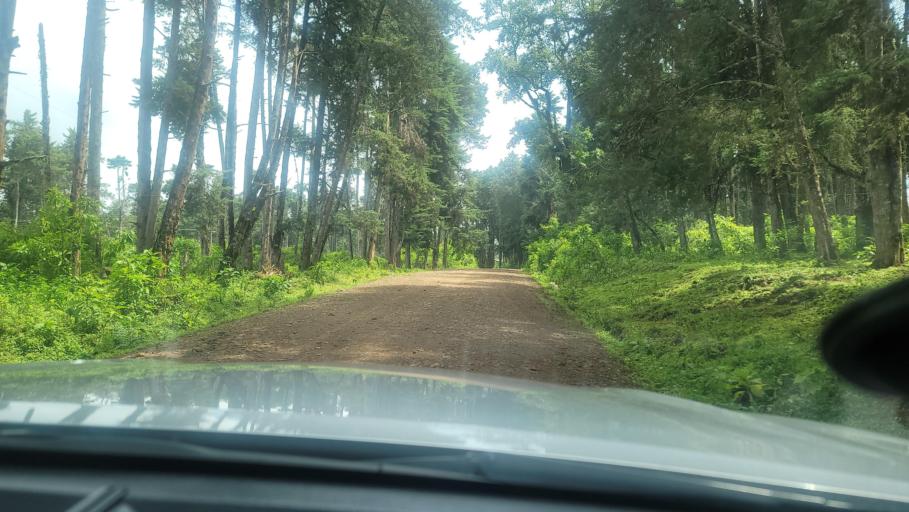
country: ET
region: Oromiya
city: Agaro
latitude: 7.7919
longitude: 36.4185
